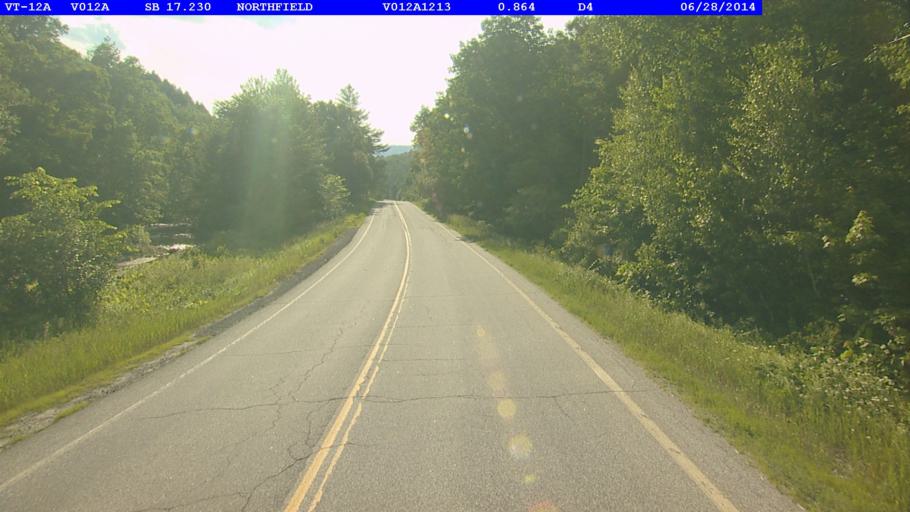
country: US
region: Vermont
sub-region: Washington County
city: Northfield
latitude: 44.1173
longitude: -72.7098
